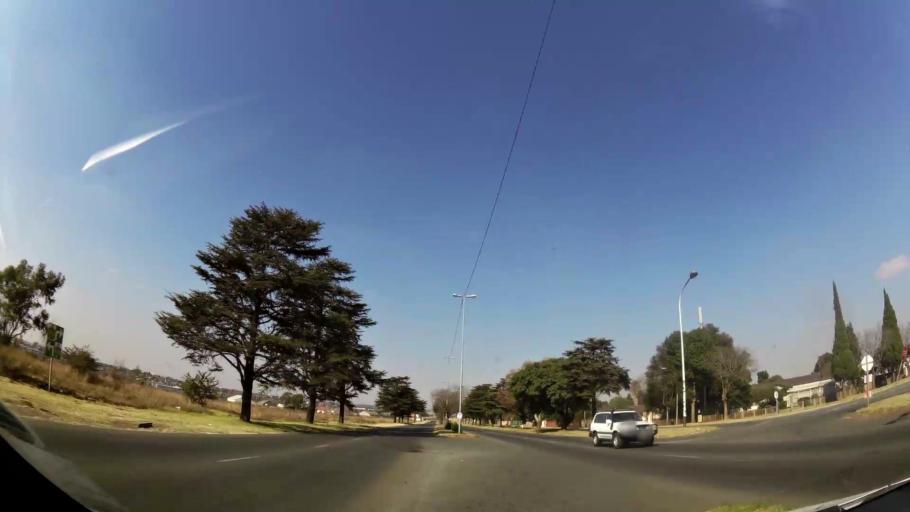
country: ZA
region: Gauteng
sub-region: Ekurhuleni Metropolitan Municipality
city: Boksburg
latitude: -26.2423
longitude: 28.2951
